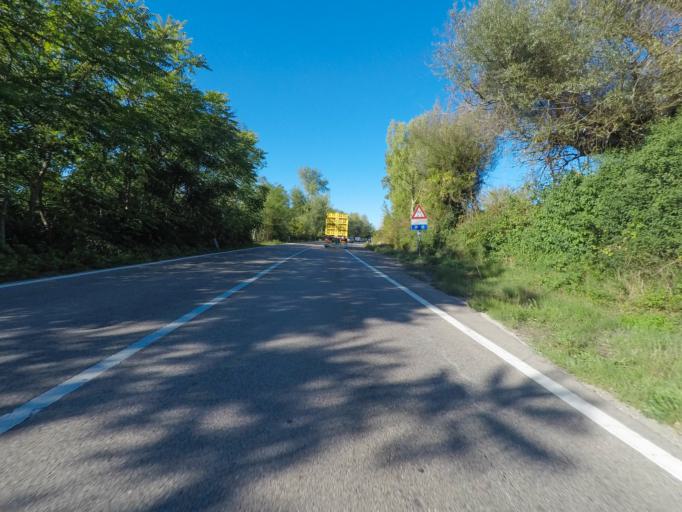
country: IT
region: Tuscany
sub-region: Provincia di Siena
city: Rosia
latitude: 43.1994
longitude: 11.2761
